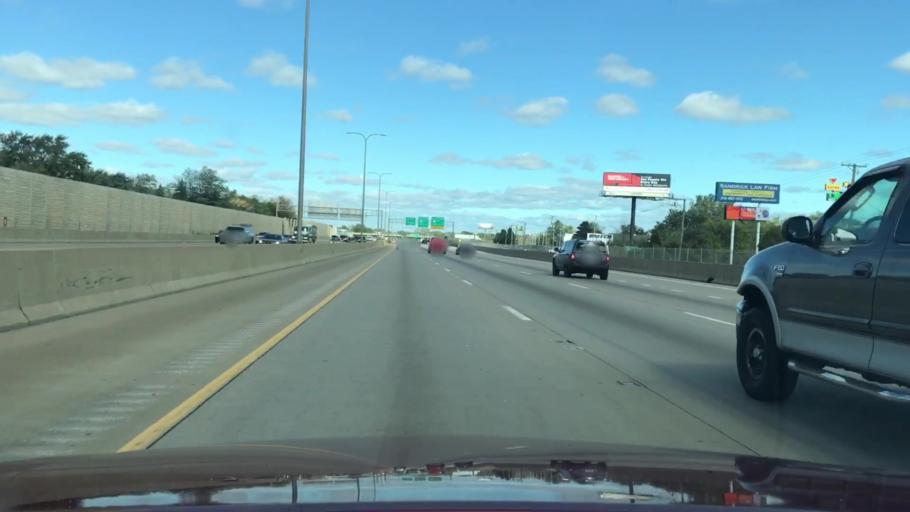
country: US
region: Illinois
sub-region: Cook County
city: South Holland
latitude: 41.5947
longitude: -87.5834
